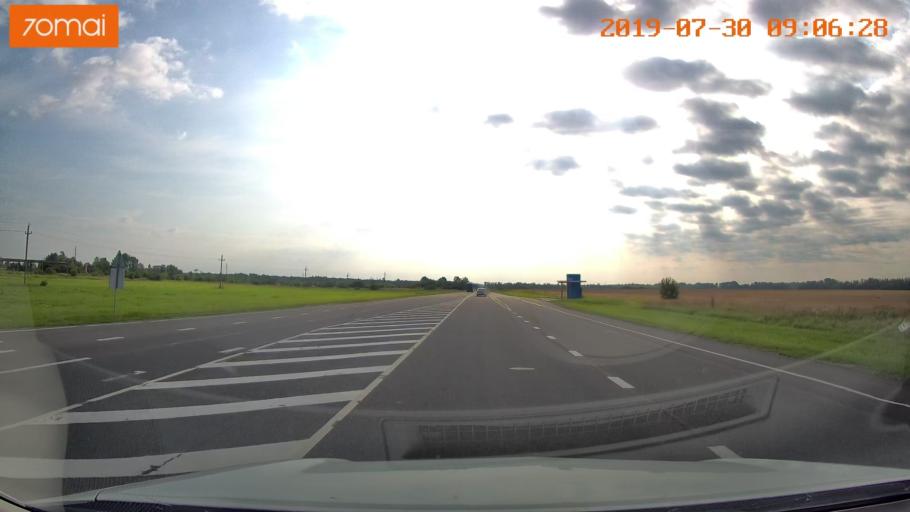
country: RU
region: Kaliningrad
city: Gusev
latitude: 54.6096
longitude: 22.3369
